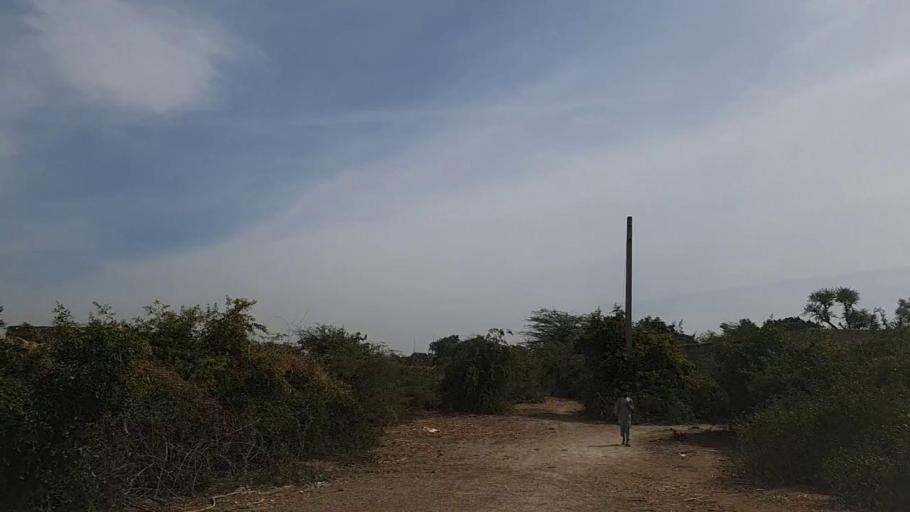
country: PK
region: Sindh
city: Samaro
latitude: 25.2907
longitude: 69.4175
